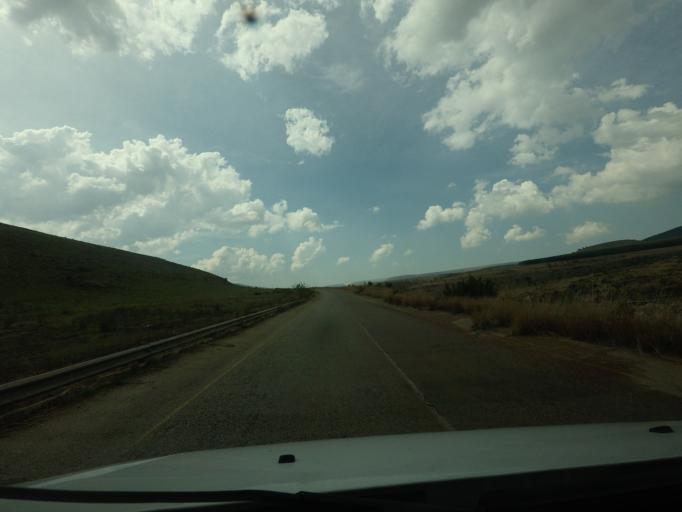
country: ZA
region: Mpumalanga
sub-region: Ehlanzeni District
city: Graksop
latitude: -24.6874
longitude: 30.8132
